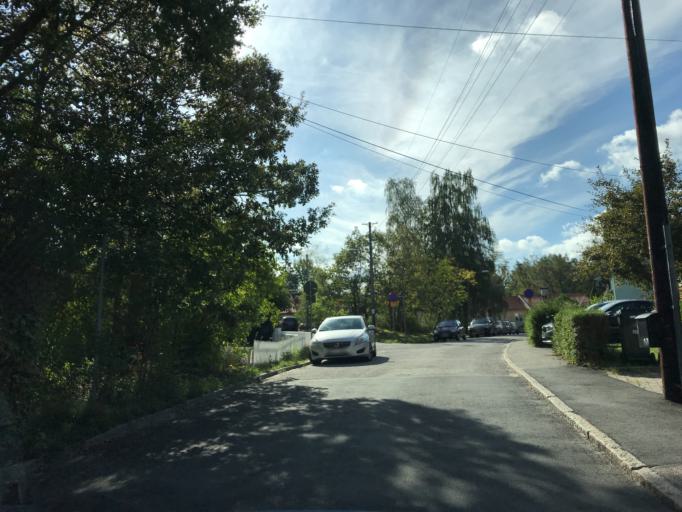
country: SE
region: Stockholm
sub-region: Huddinge Kommun
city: Segeltorp
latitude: 59.2769
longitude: 17.9713
